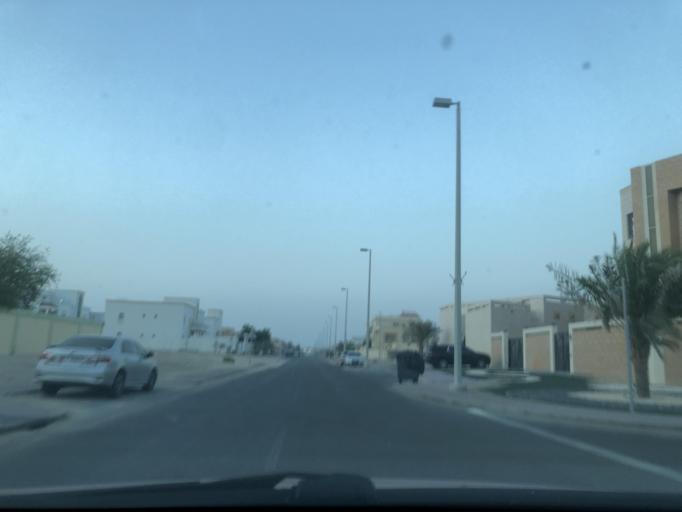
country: AE
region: Abu Dhabi
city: Abu Dhabi
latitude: 24.3527
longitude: 54.6268
